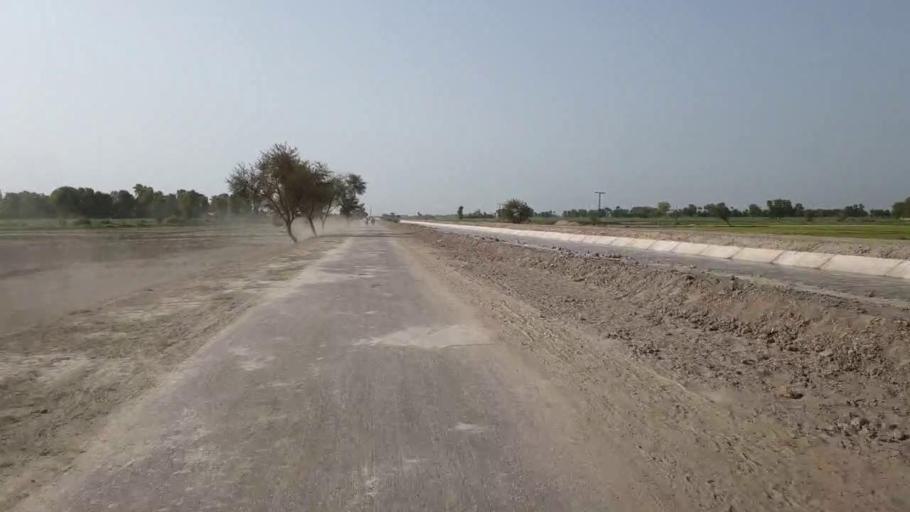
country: PK
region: Sindh
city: Daur
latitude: 26.3334
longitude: 68.1643
